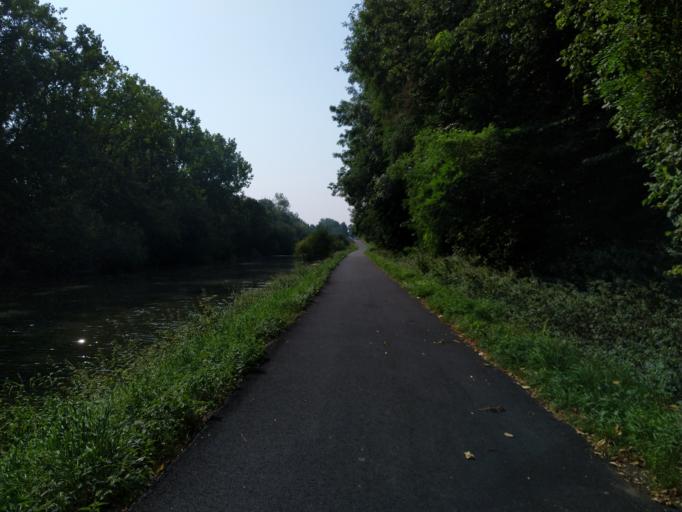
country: BE
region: Wallonia
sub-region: Province du Hainaut
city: Seneffe
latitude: 50.5266
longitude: 4.2598
